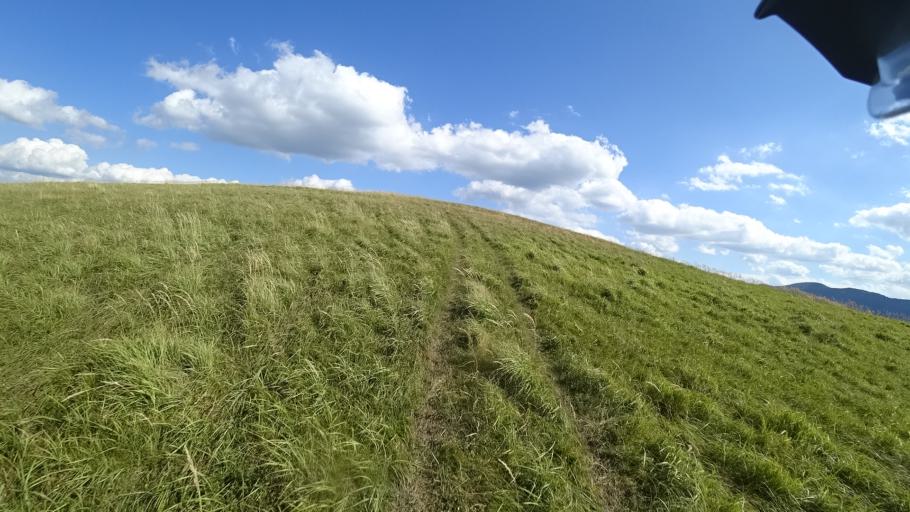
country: HR
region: Zadarska
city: Gracac
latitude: 44.3887
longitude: 16.0284
